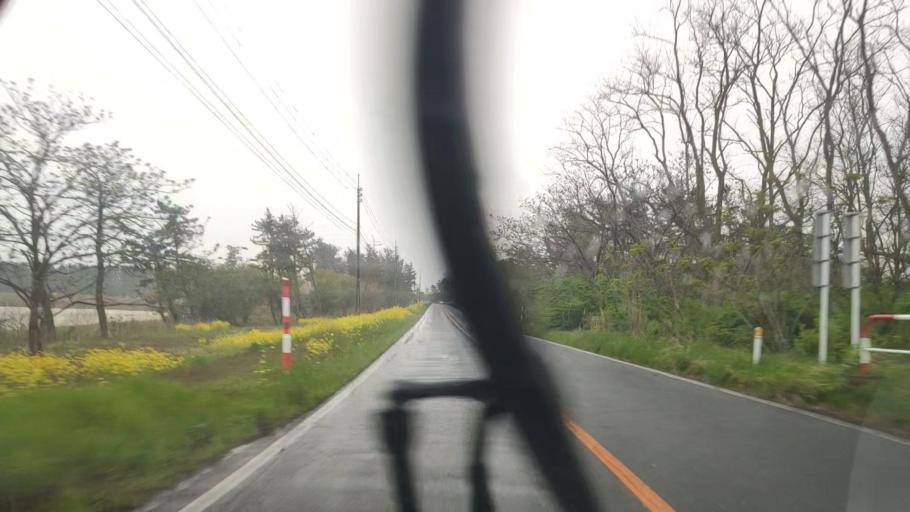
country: JP
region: Akita
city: Tenno
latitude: 40.0362
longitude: 139.9533
